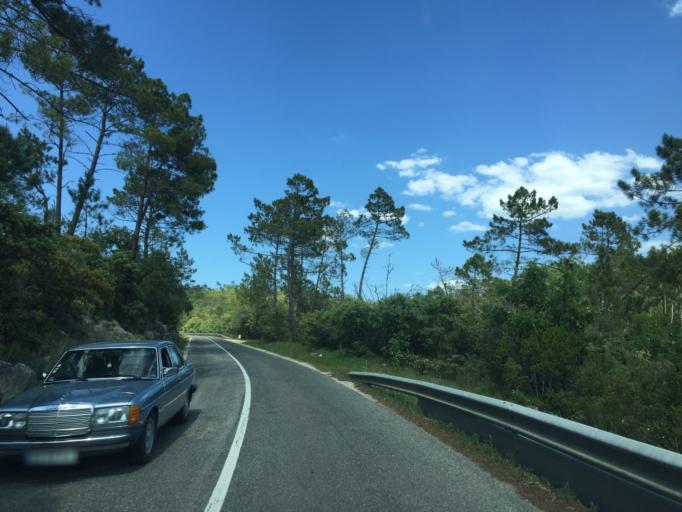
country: PT
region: Leiria
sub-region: Alvaiazere
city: Alvaiazere
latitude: 39.7823
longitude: -8.4482
